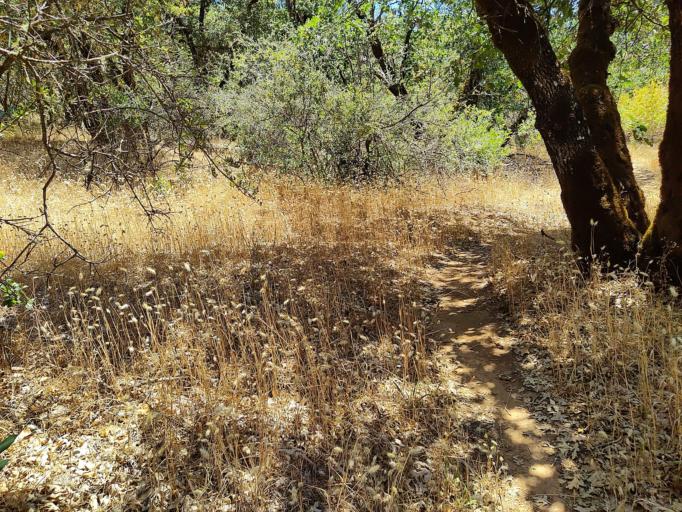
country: US
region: California
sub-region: Placer County
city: Meadow Vista
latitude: 39.0262
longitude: -120.9897
